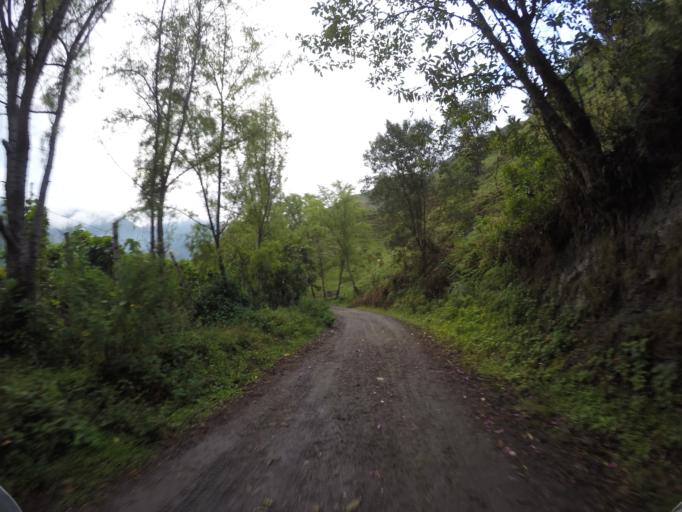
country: CO
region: Tolima
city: Cajamarca
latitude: 4.5115
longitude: -75.4032
